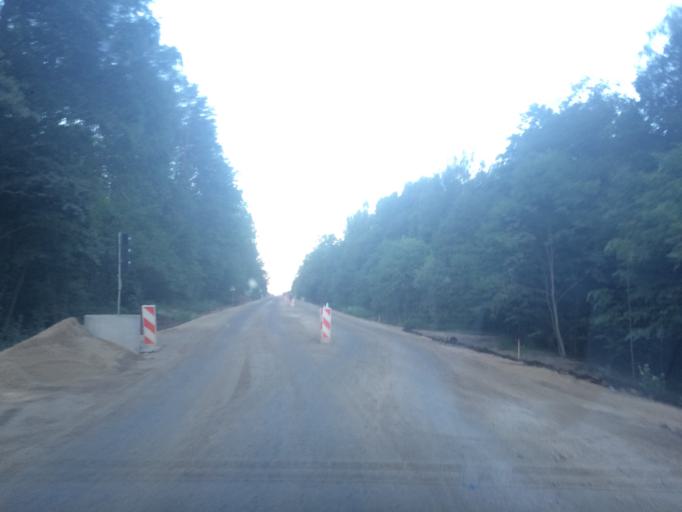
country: LT
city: Zarasai
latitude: 55.7578
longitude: 26.3282
